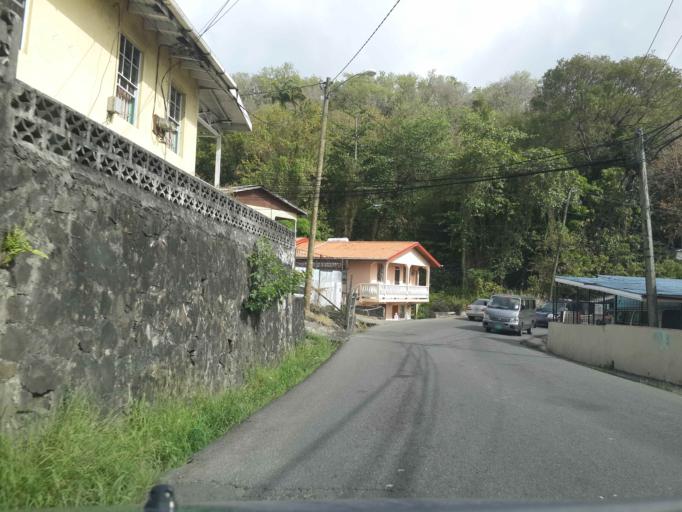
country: LC
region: Castries Quarter
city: Bisee
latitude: 14.0168
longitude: -60.9862
